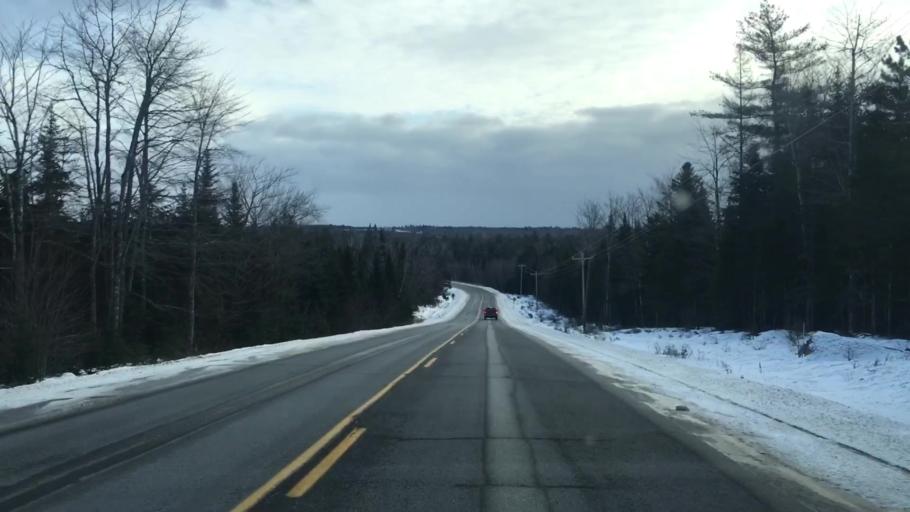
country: US
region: Maine
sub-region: Washington County
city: Machias
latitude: 44.9994
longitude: -67.5906
